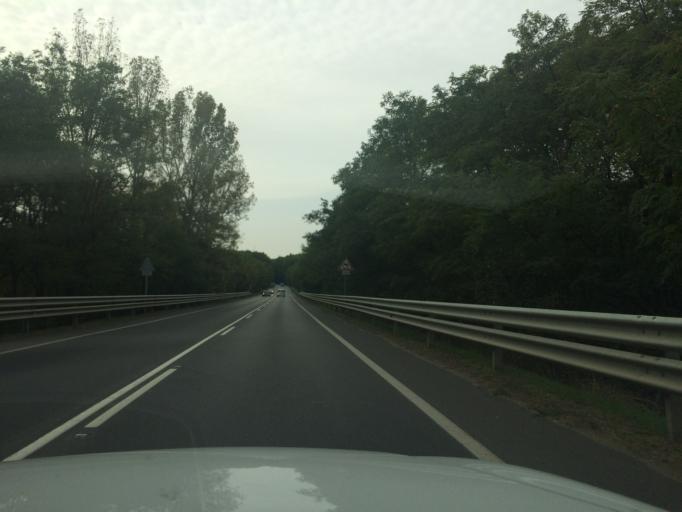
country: HU
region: Szabolcs-Szatmar-Bereg
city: Nyiregyhaza
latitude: 47.9903
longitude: 21.7237
